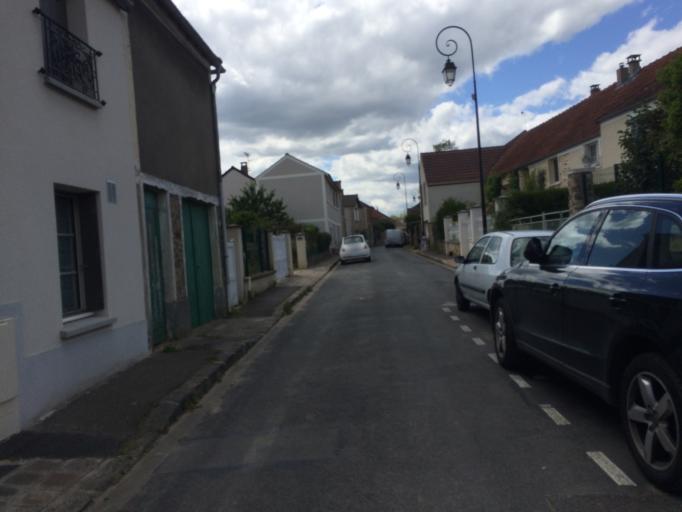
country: FR
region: Ile-de-France
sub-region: Departement de l'Essonne
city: Les Ulis
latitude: 48.6712
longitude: 2.1694
